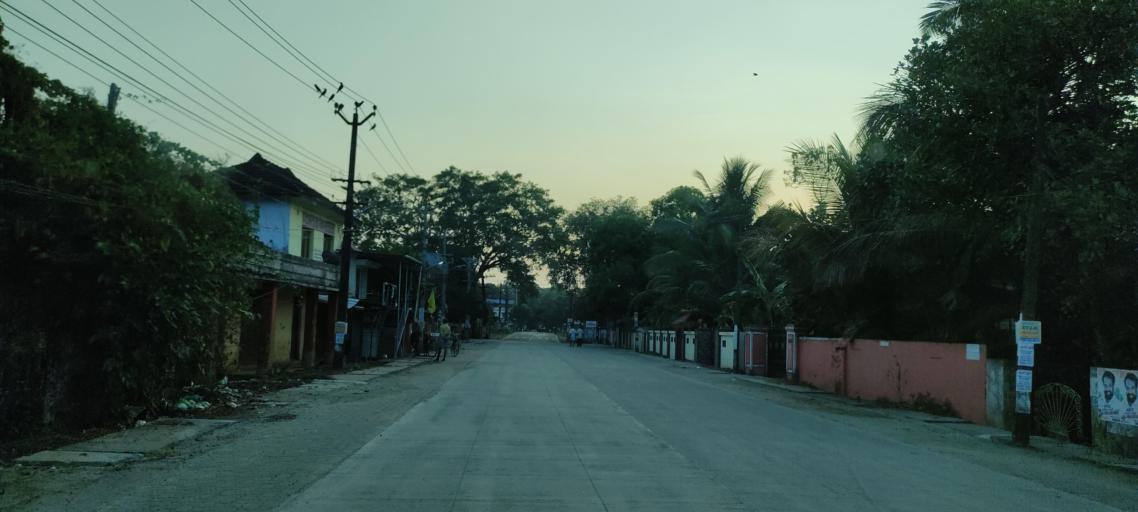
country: IN
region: Kerala
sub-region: Alappuzha
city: Alleppey
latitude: 9.4664
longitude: 76.3404
